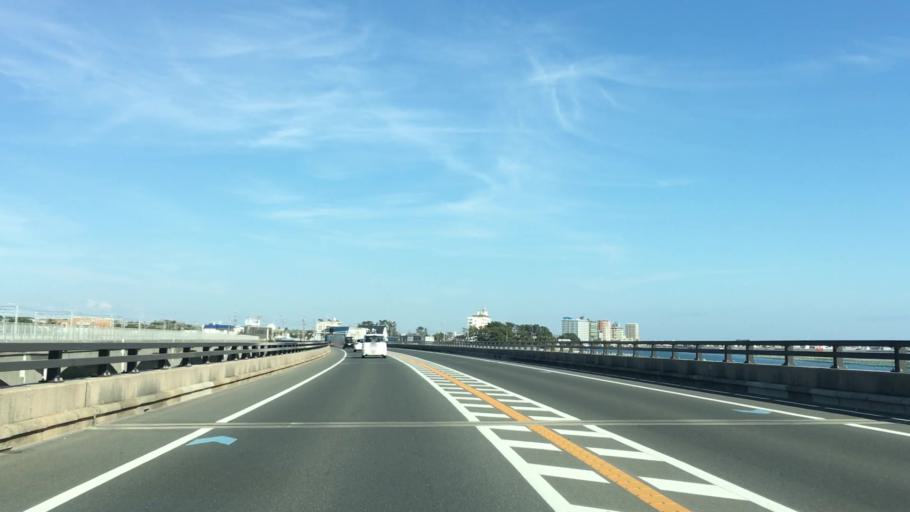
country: JP
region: Shizuoka
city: Kosai-shi
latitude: 34.6938
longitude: 137.5861
